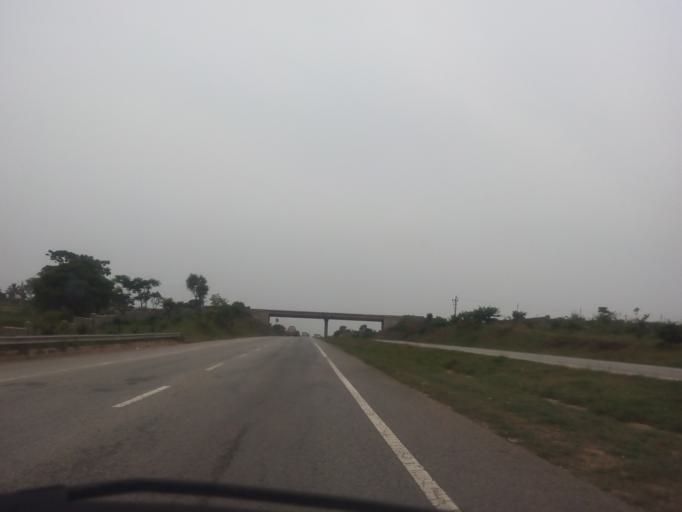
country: IN
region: Karnataka
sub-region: Bangalore Urban
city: Bangalore
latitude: 12.9728
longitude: 77.4714
